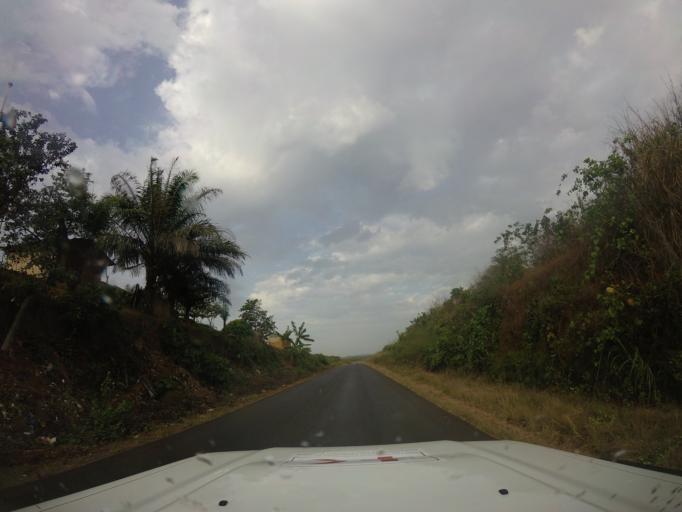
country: LR
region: Bomi
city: Tubmanburg
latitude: 6.7273
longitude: -11.0376
